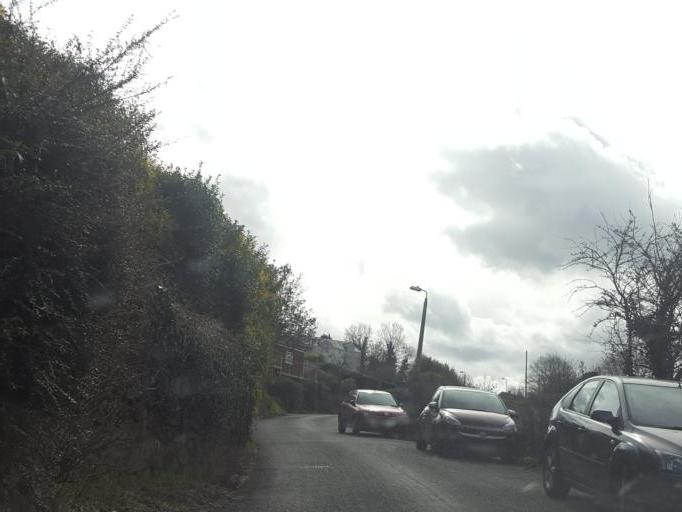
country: GB
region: England
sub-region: Worcestershire
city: Great Malvern
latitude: 52.1218
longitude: -2.3456
